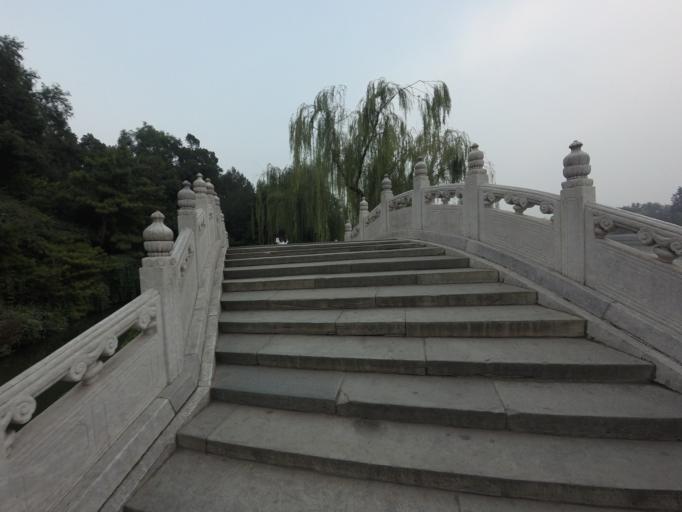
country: CN
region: Beijing
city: Jingshan
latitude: 39.9239
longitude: 116.3815
